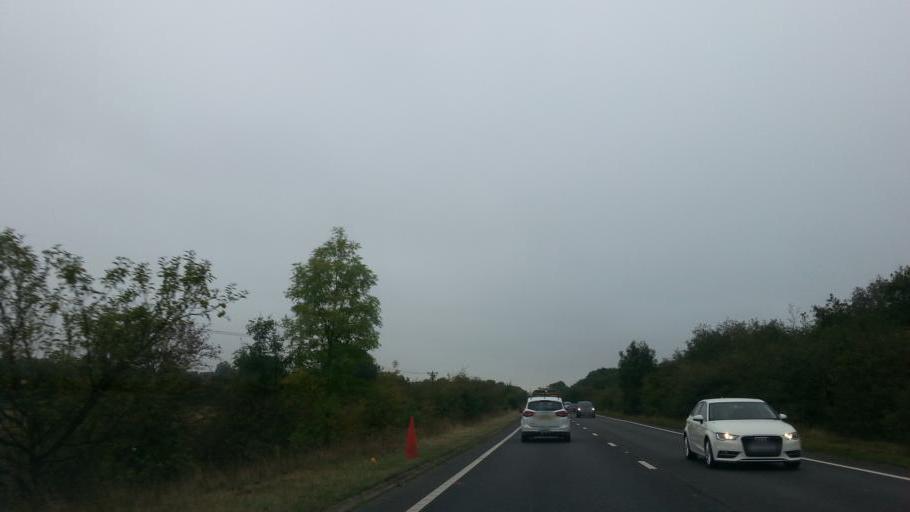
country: GB
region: England
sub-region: Northamptonshire
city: Stanwick
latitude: 52.3431
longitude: -0.5683
